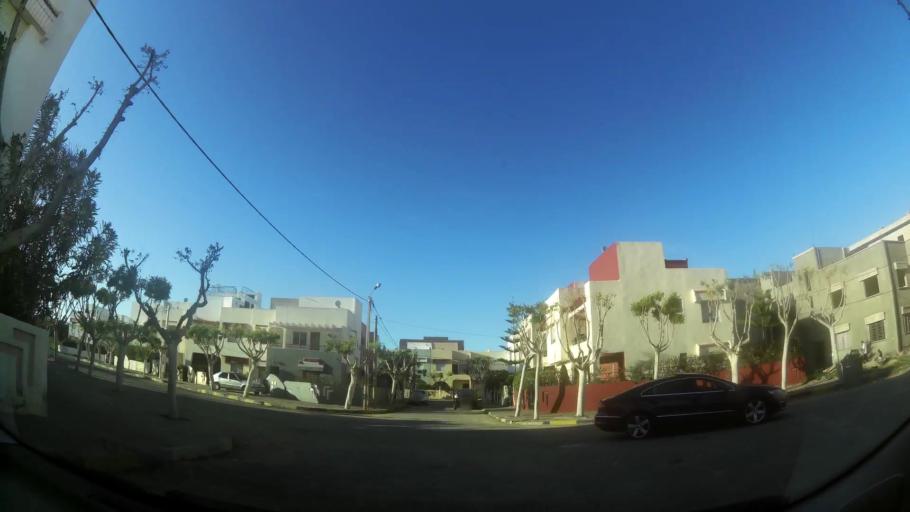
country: MA
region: Oriental
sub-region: Berkane-Taourirt
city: Madagh
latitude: 35.0865
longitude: -2.2496
